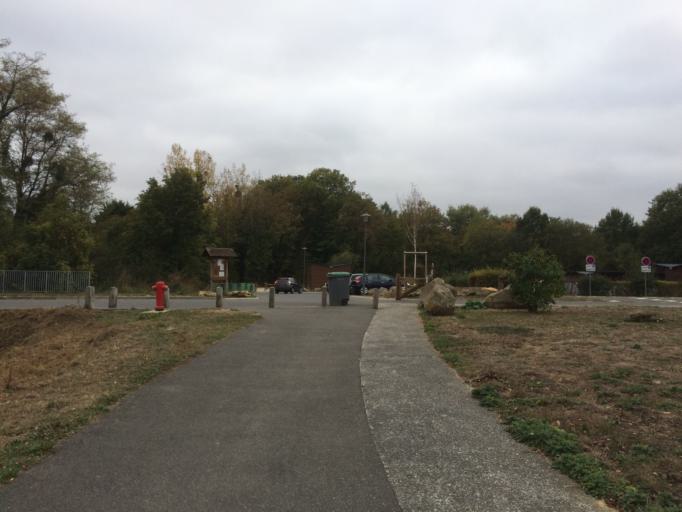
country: FR
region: Ile-de-France
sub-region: Departement de l'Essonne
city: Courcouronnes
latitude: 48.6244
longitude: 2.4015
